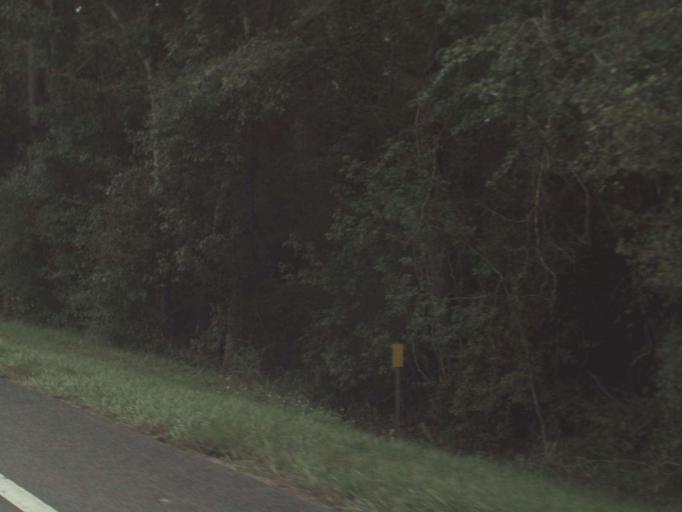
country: US
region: Florida
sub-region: Walton County
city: DeFuniak Springs
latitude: 30.6890
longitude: -85.9365
